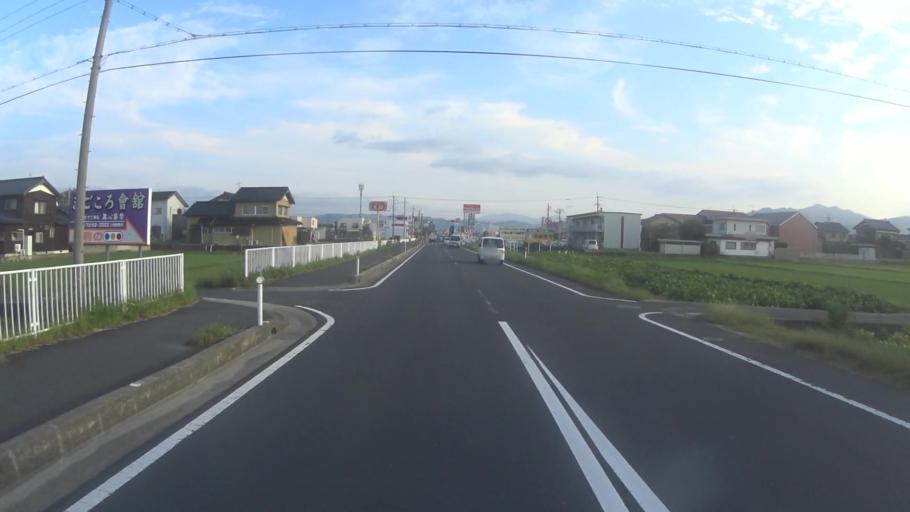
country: JP
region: Kyoto
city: Miyazu
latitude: 35.6191
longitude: 135.0753
